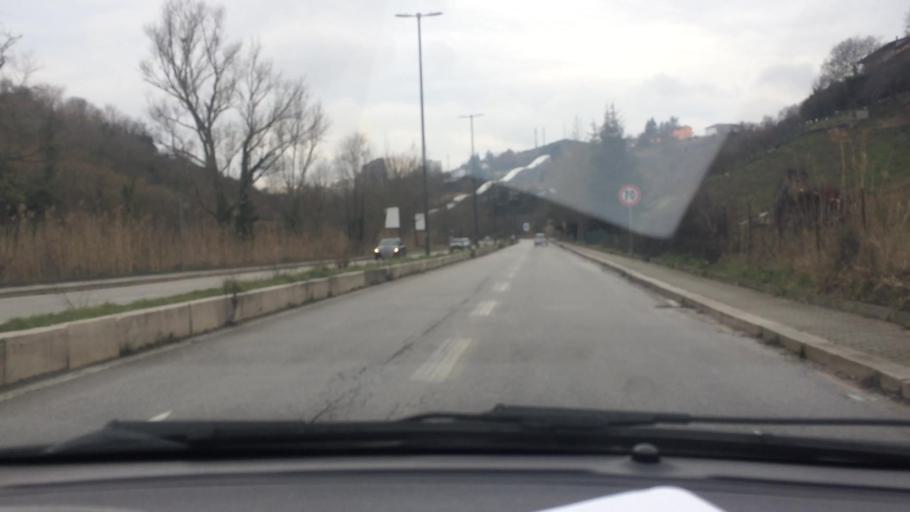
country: IT
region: Basilicate
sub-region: Provincia di Potenza
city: Potenza
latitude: 40.6413
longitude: 15.7991
